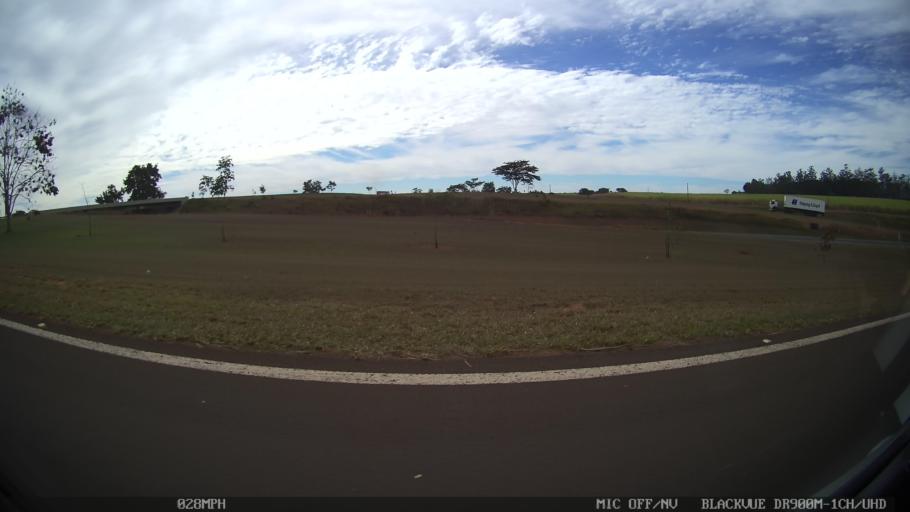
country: BR
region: Sao Paulo
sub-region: Santa Adelia
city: Santa Adelia
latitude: -21.2780
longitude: -48.8601
